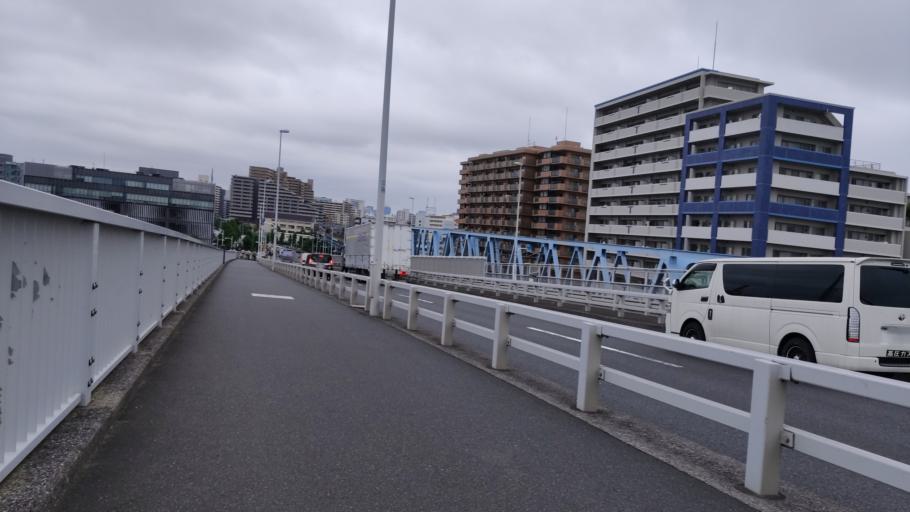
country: JP
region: Tokyo
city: Urayasu
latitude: 35.6656
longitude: 139.8432
